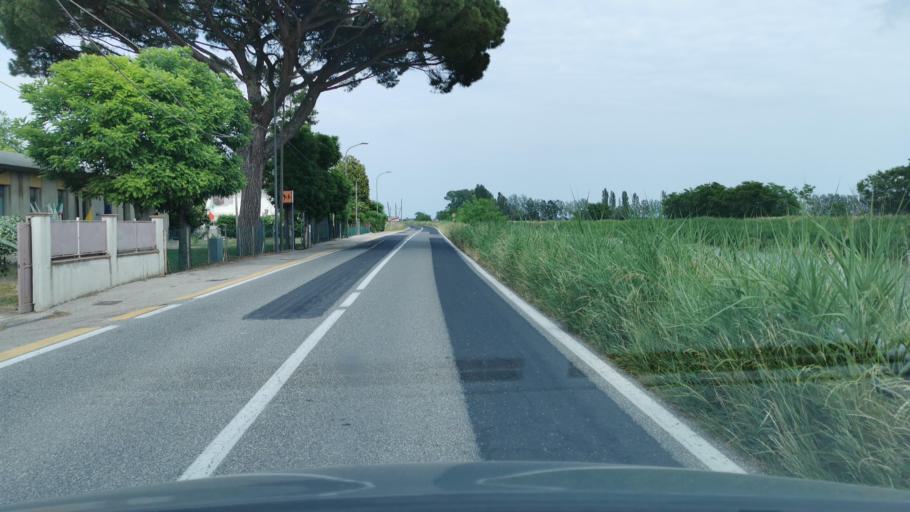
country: IT
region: Emilia-Romagna
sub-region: Provincia di Ravenna
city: Marina Romea
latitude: 44.5545
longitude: 12.2281
